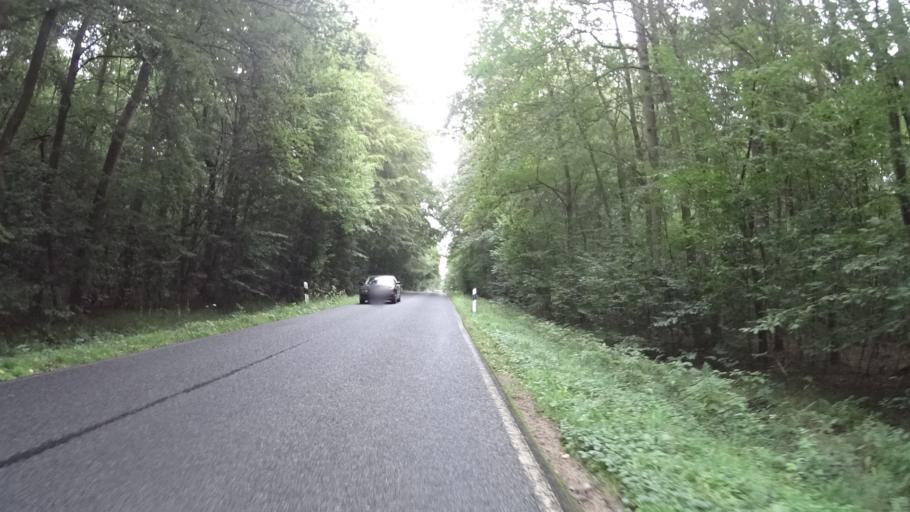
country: DE
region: Schleswig-Holstein
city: Nusse
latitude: 53.6850
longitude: 10.5931
